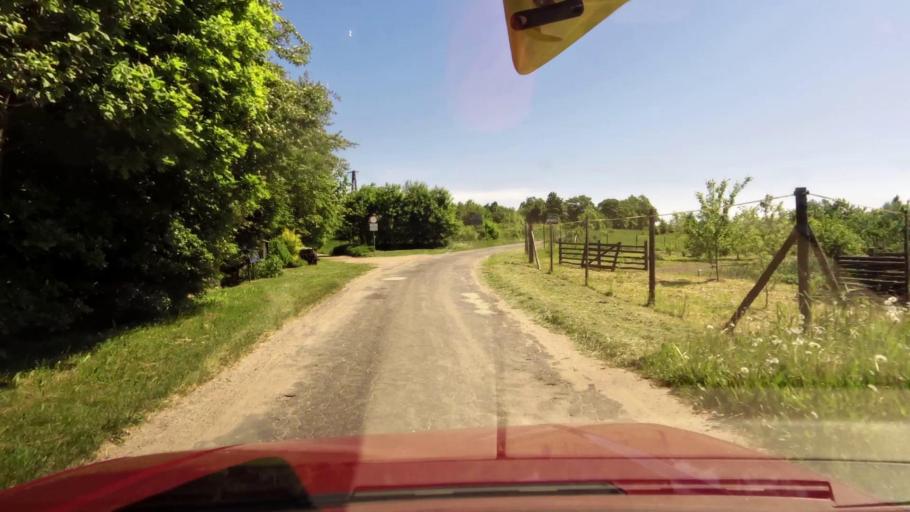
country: PL
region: West Pomeranian Voivodeship
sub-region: Powiat koszalinski
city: Polanow
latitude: 54.0441
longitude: 16.7452
